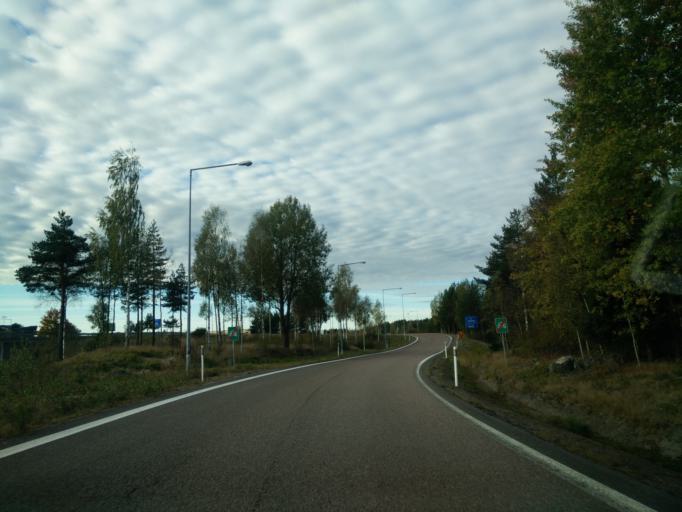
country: SE
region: Gaevleborg
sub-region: Soderhamns Kommun
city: Soderhamn
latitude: 61.2982
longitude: 17.0246
